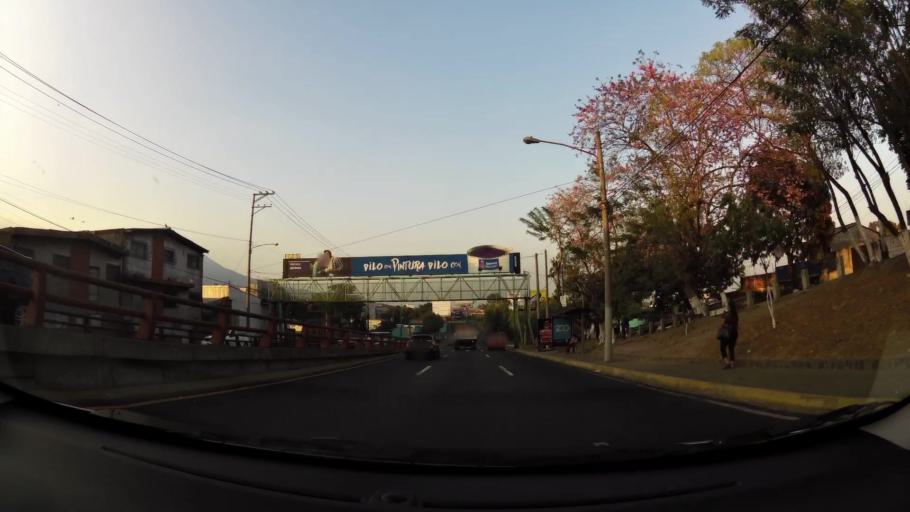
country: SV
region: San Salvador
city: San Salvador
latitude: 13.6885
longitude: -89.2174
